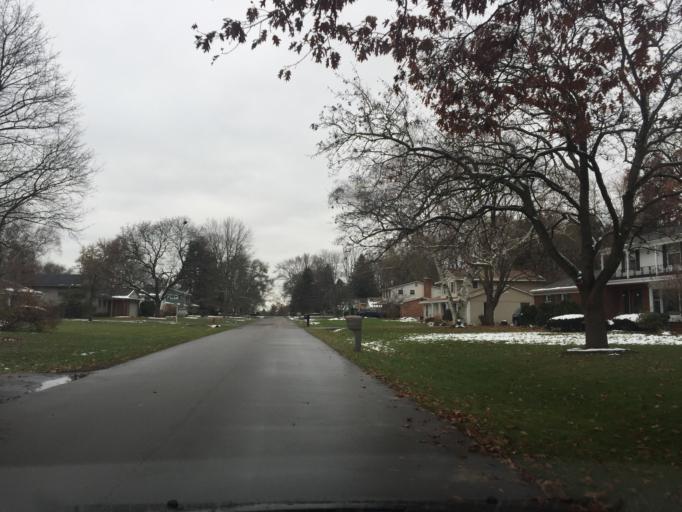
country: US
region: Michigan
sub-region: Oakland County
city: Franklin
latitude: 42.5424
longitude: -83.2919
